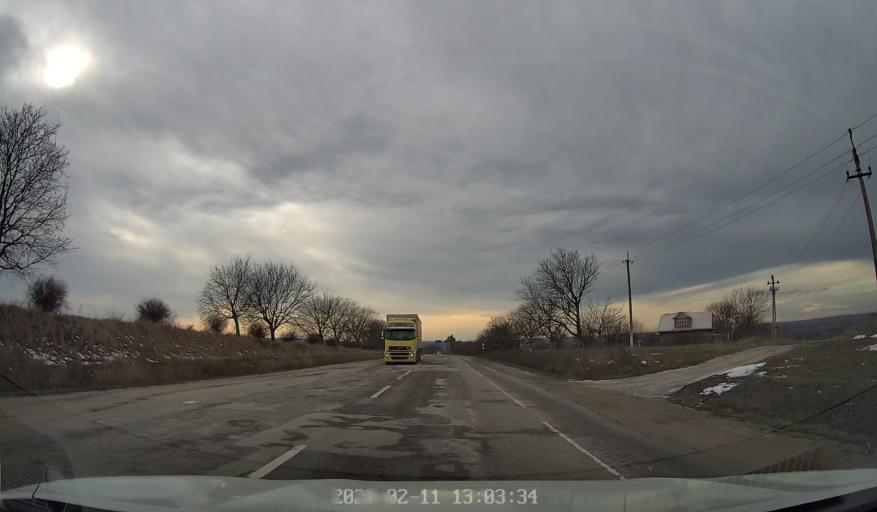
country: MD
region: Briceni
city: Briceni
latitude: 48.3111
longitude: 26.9570
